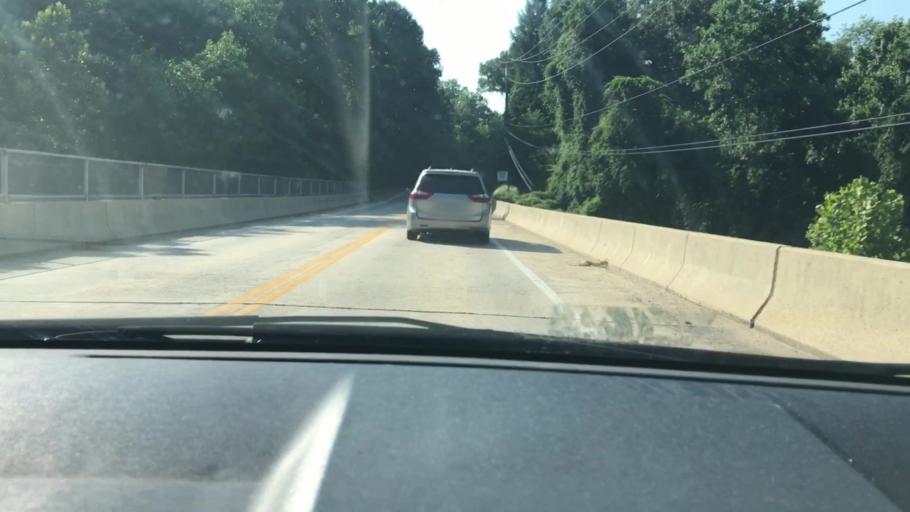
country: US
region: Virginia
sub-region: Fairfax County
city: Great Falls
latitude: 38.9753
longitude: -77.2551
